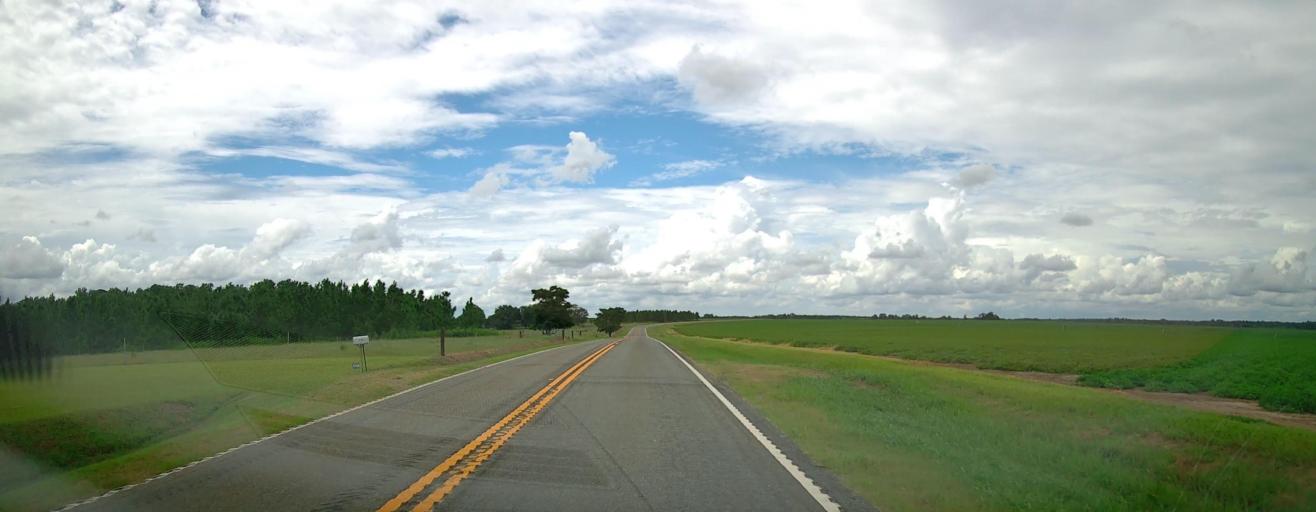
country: US
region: Georgia
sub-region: Dooly County
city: Unadilla
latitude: 32.2608
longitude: -83.8056
